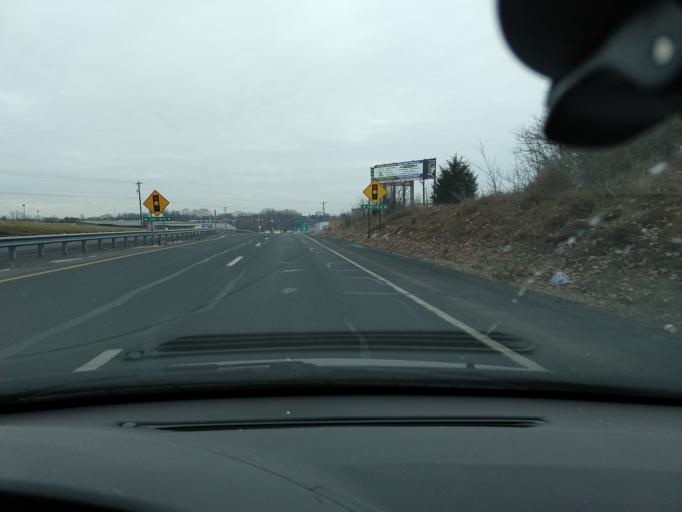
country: US
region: Pennsylvania
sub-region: Berks County
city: New Berlinville
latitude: 40.3362
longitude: -75.6215
